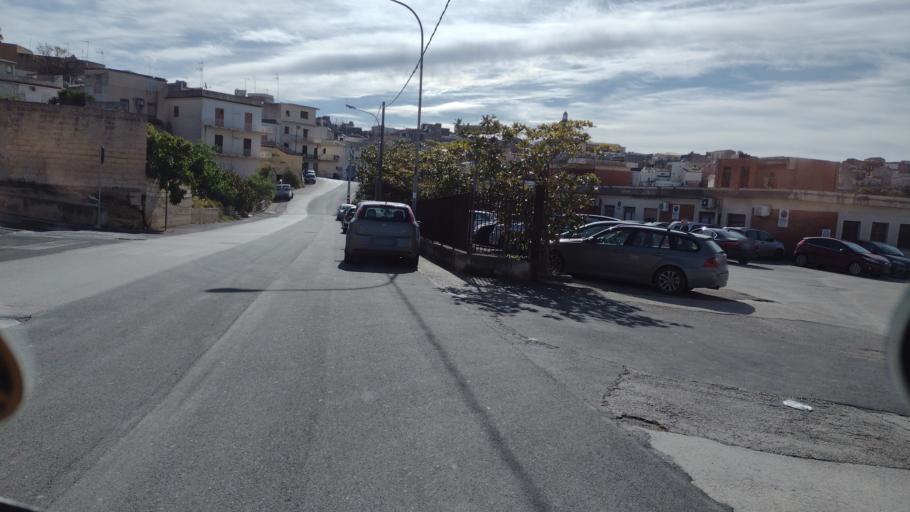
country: IT
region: Sicily
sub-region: Provincia di Siracusa
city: Noto
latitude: 36.8971
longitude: 15.0684
